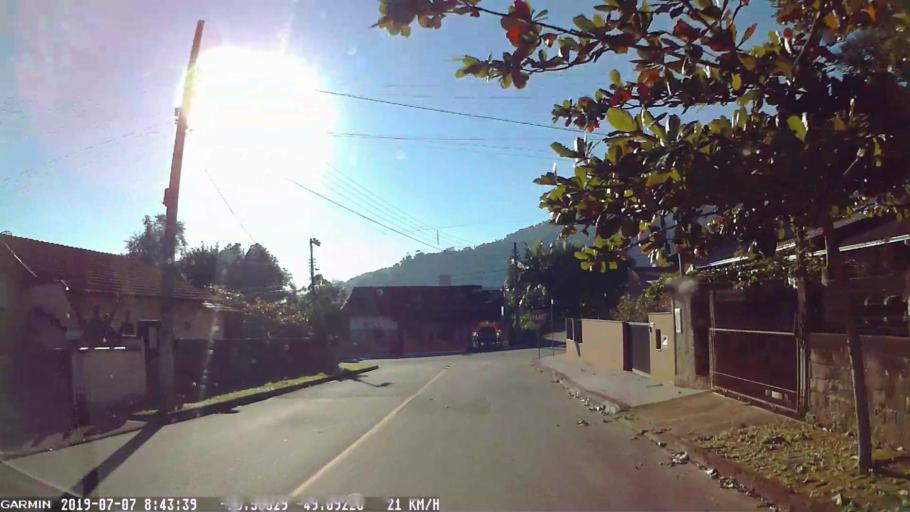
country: BR
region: Santa Catarina
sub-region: Jaragua Do Sul
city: Jaragua do Sul
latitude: -26.5083
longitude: -49.0922
